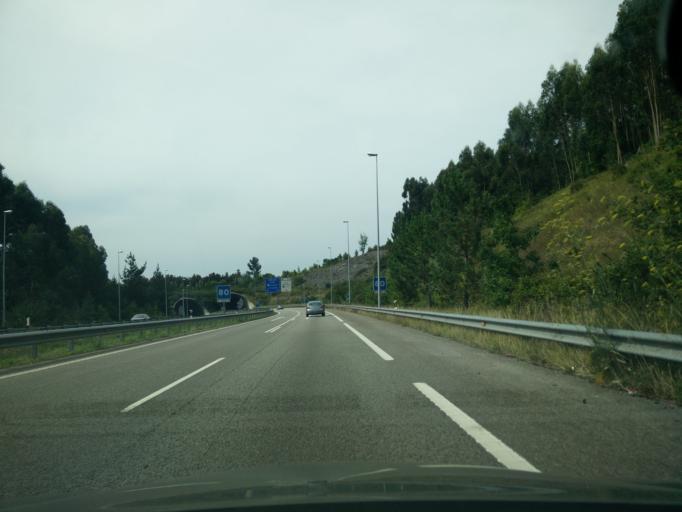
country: ES
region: Asturias
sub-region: Province of Asturias
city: Arriba
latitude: 43.5075
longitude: -5.5951
